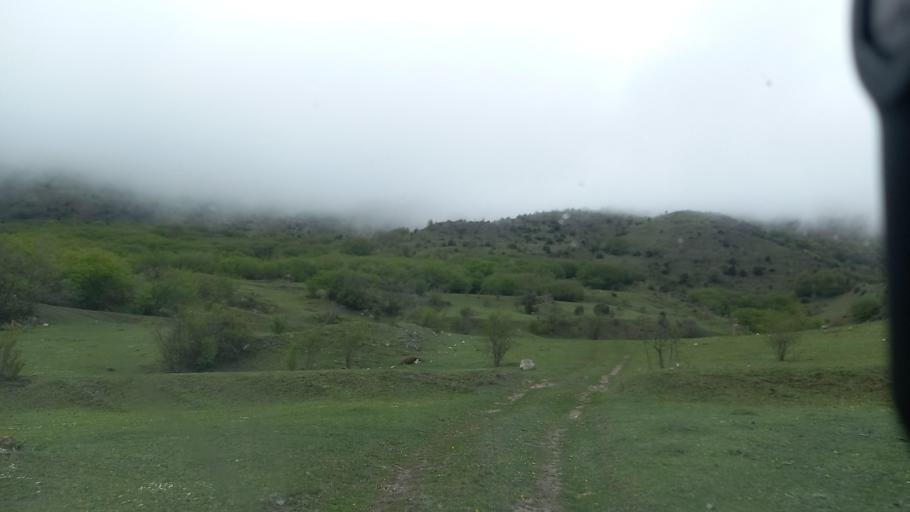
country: RU
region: Kabardino-Balkariya
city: Verkhnyaya Balkariya
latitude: 43.1688
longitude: 43.5000
